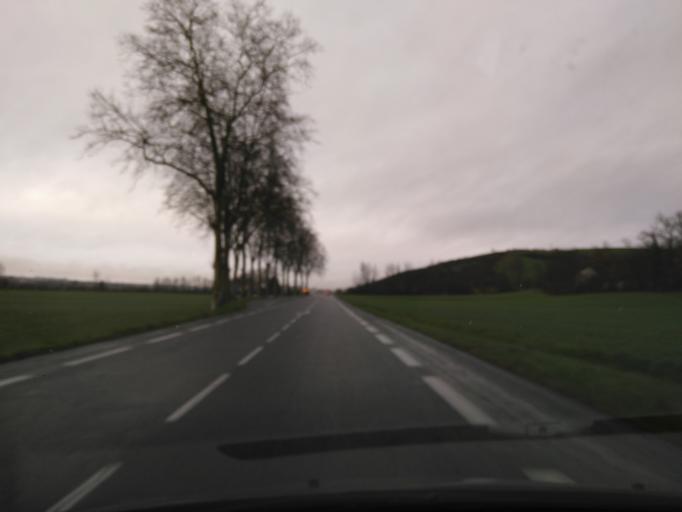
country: FR
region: Midi-Pyrenees
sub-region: Departement de la Haute-Garonne
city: Rieux-Volvestre
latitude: 43.2337
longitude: 1.2076
